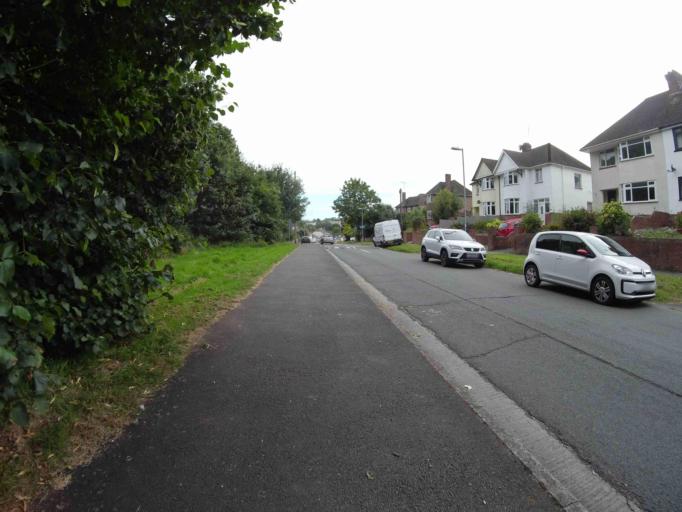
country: GB
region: England
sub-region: Devon
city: Heavitree
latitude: 50.7238
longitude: -3.4921
